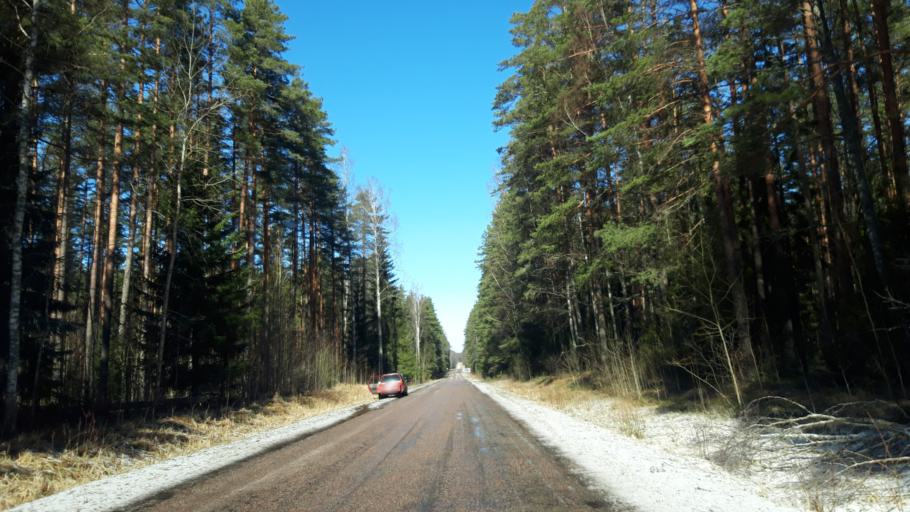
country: LV
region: Strenci
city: Strenci
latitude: 57.5962
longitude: 25.7187
